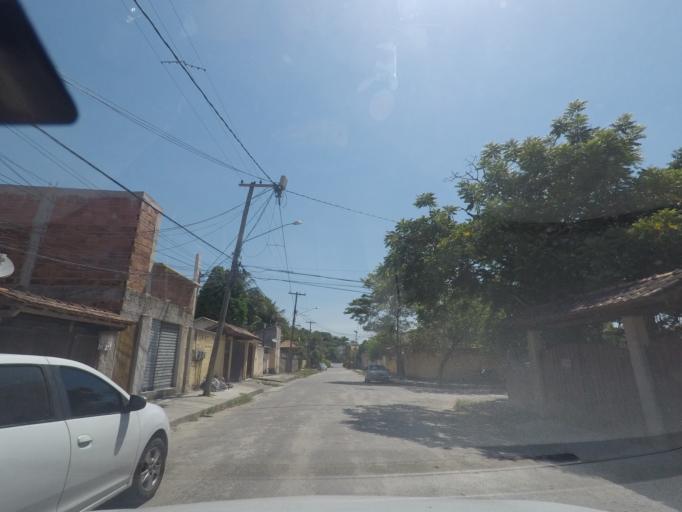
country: BR
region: Rio de Janeiro
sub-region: Niteroi
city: Niteroi
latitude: -22.9301
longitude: -43.0090
